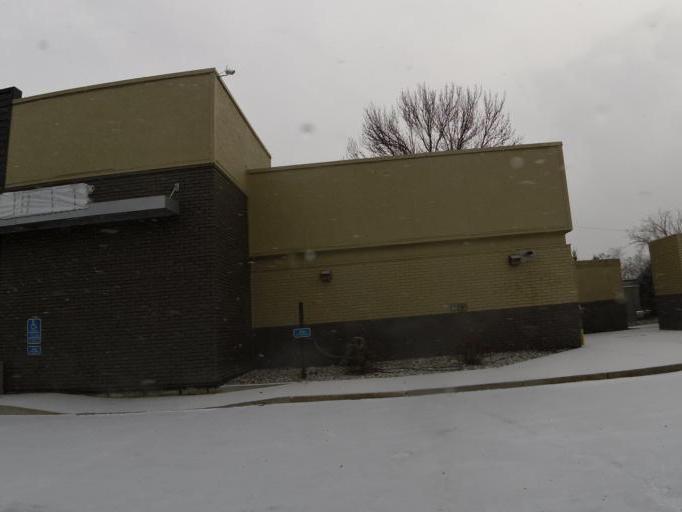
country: US
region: Minnesota
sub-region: Dakota County
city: Mendota Heights
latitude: 44.9165
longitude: -93.1426
